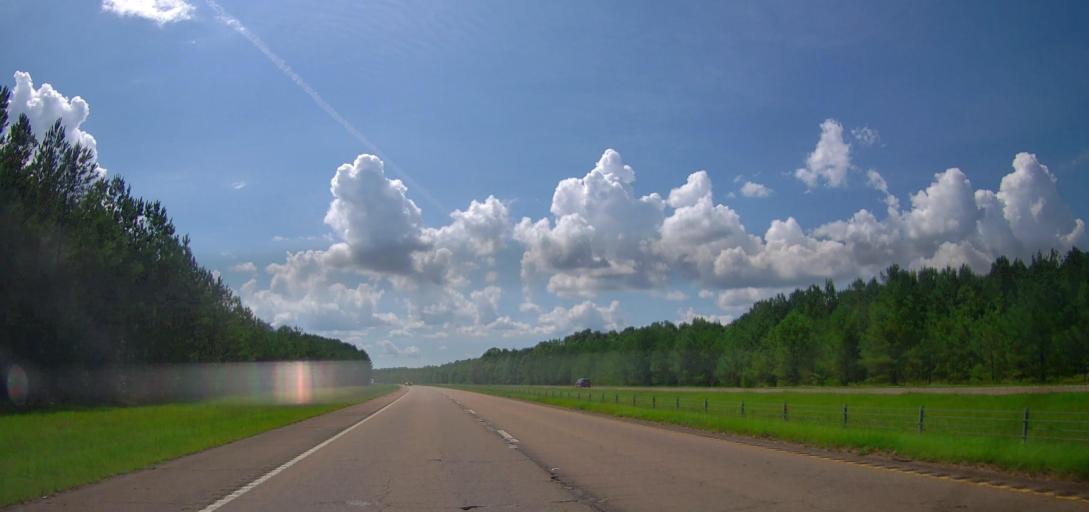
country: US
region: Mississippi
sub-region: Lowndes County
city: New Hope
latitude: 33.5073
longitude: -88.3198
